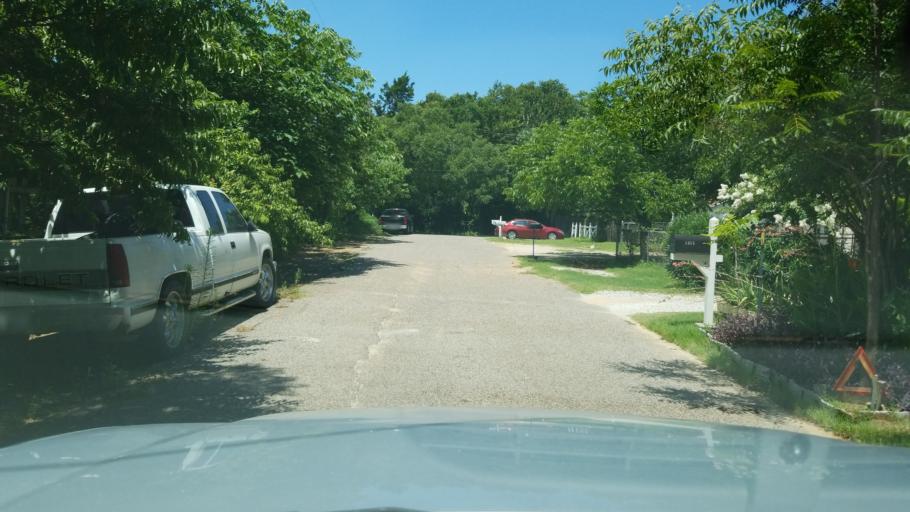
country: US
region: Texas
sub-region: Dallas County
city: Irving
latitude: 32.8055
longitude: -96.9238
